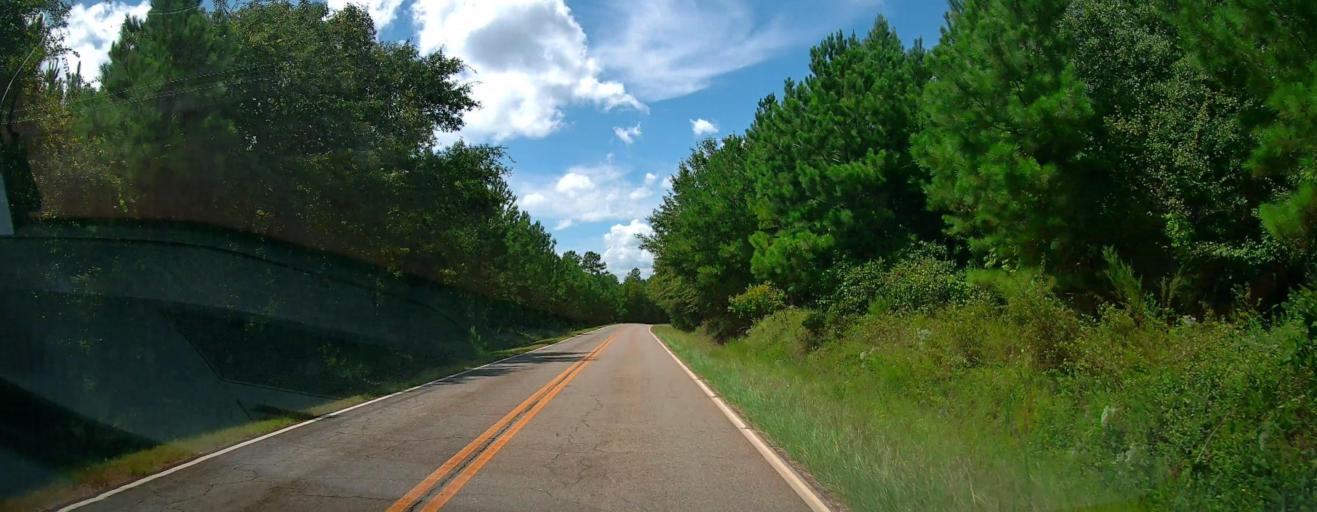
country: US
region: Georgia
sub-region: Peach County
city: Fort Valley
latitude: 32.5332
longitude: -83.8068
